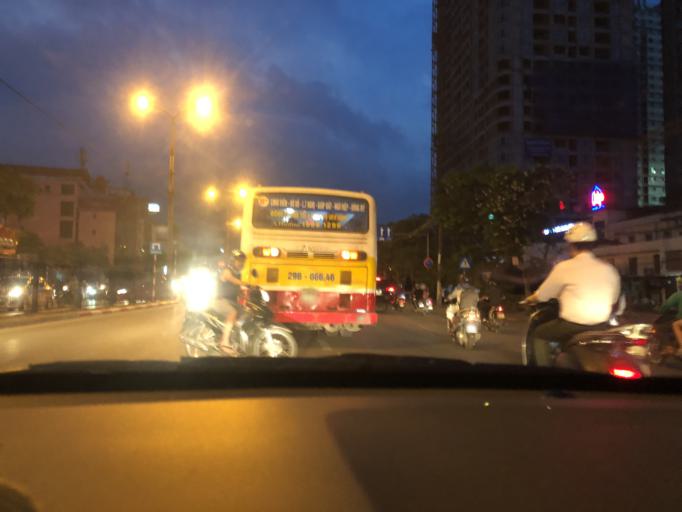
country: VN
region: Ha Noi
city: Hai BaTrung
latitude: 20.9871
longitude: 105.8411
